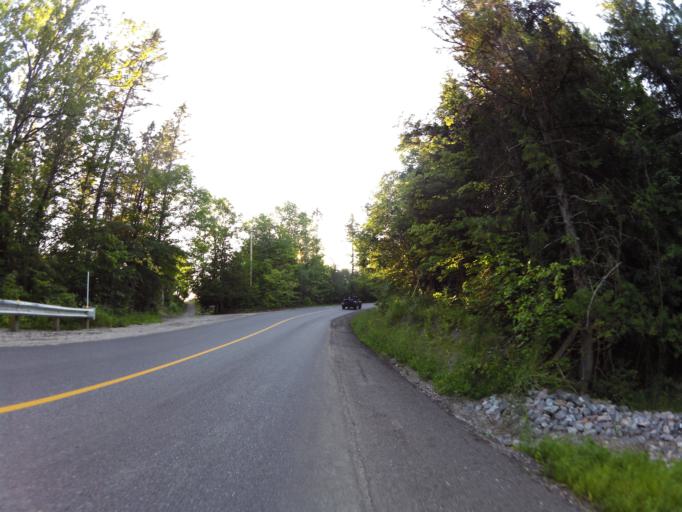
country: CA
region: Quebec
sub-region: Outaouais
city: Wakefield
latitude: 45.6840
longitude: -75.9365
